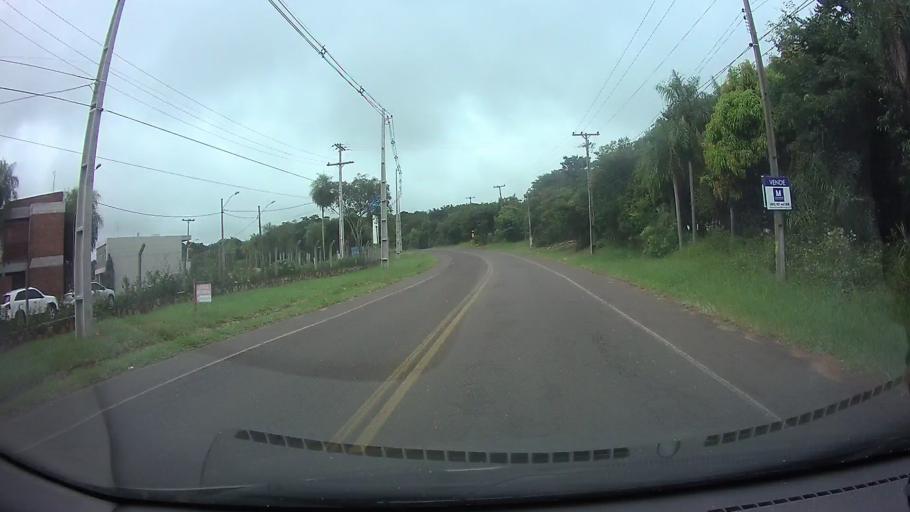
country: PY
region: Cordillera
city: Altos
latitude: -25.2869
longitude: -57.2641
